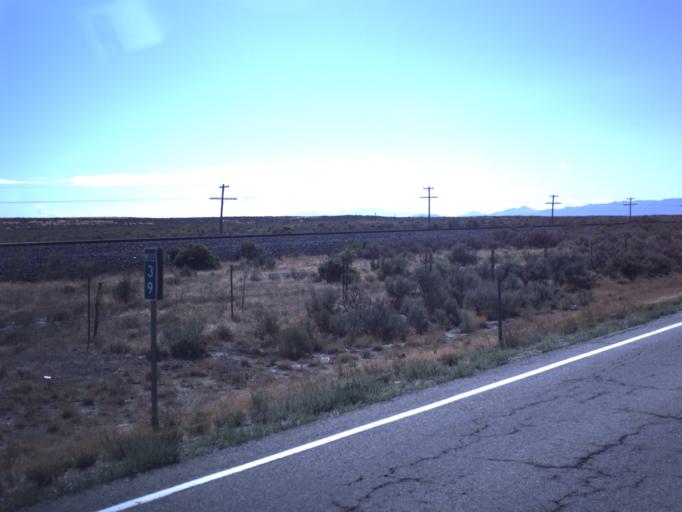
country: US
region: Utah
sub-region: Tooele County
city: Tooele
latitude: 40.3407
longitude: -112.4103
